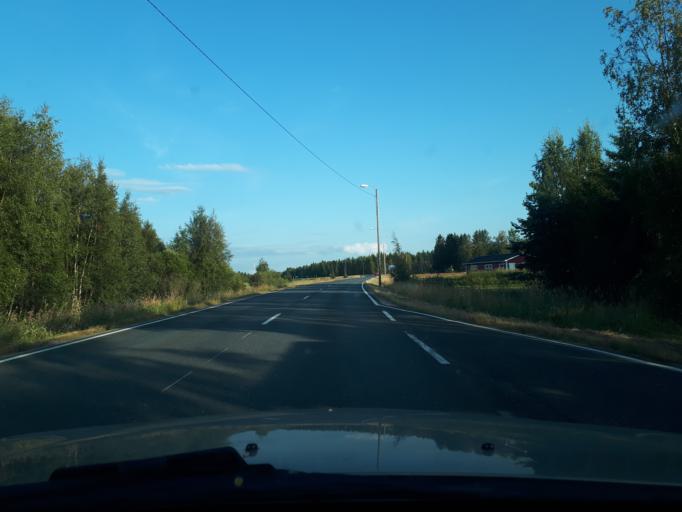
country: FI
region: Northern Ostrobothnia
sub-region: Oulu
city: Oulunsalo
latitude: 64.9827
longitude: 25.2701
